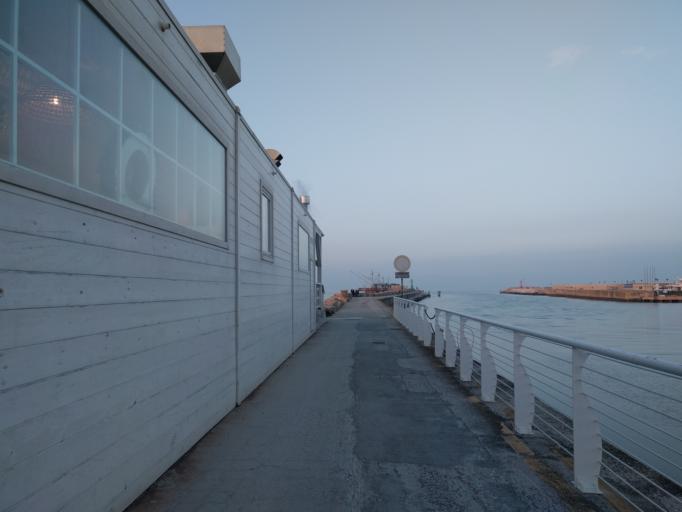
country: IT
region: The Marches
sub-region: Provincia di Pesaro e Urbino
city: Fano
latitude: 43.8525
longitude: 13.0149
